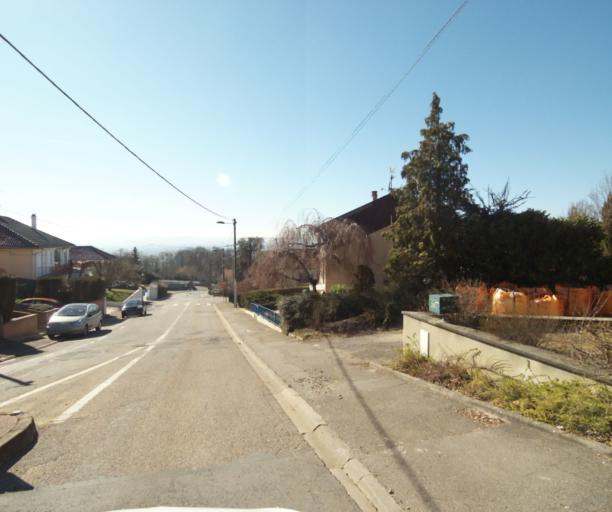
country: FR
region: Lorraine
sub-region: Departement de Meurthe-et-Moselle
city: Essey-les-Nancy
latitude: 48.7111
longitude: 6.2225
